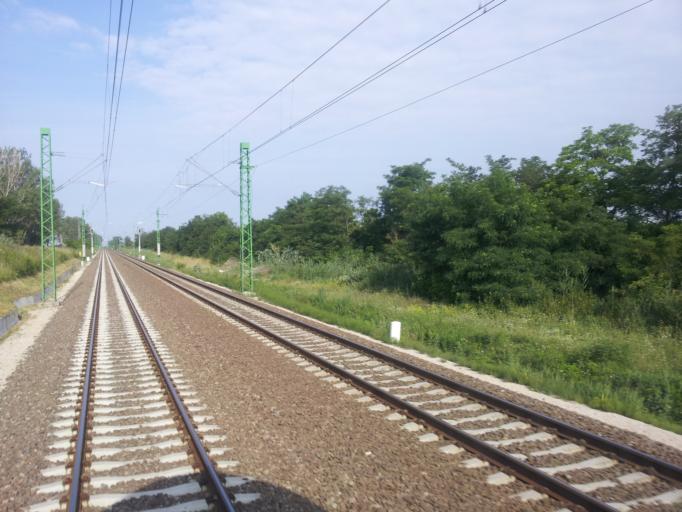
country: HU
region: Fejer
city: Pakozd
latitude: 47.1743
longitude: 18.5181
